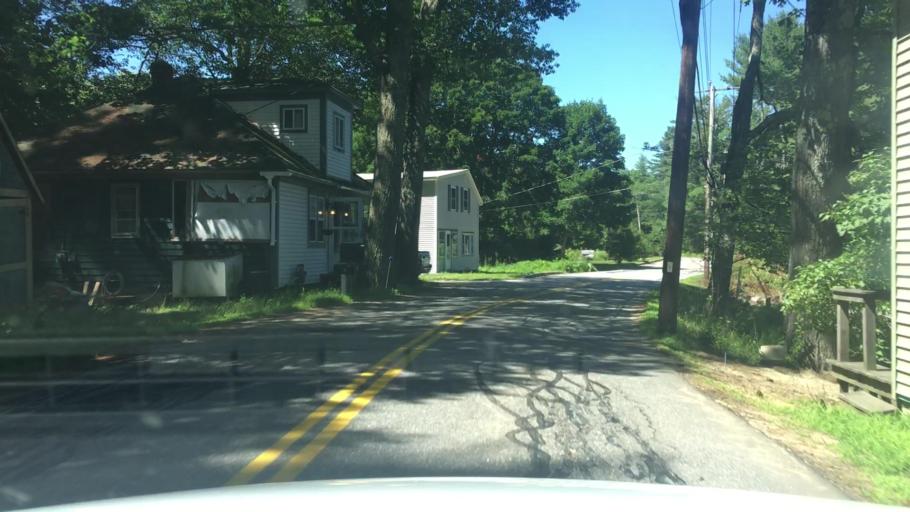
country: US
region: New Hampshire
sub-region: Merrimack County
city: Boscawen
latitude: 43.2622
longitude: -71.6193
